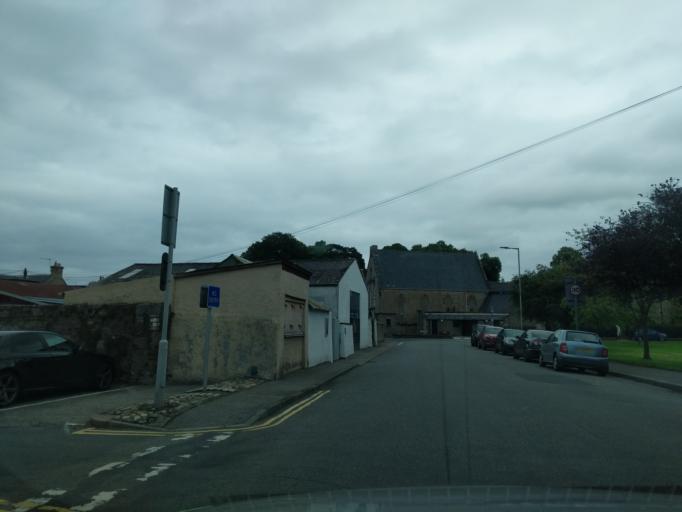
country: GB
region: Scotland
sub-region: Moray
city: Forres
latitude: 57.6082
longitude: -3.6111
